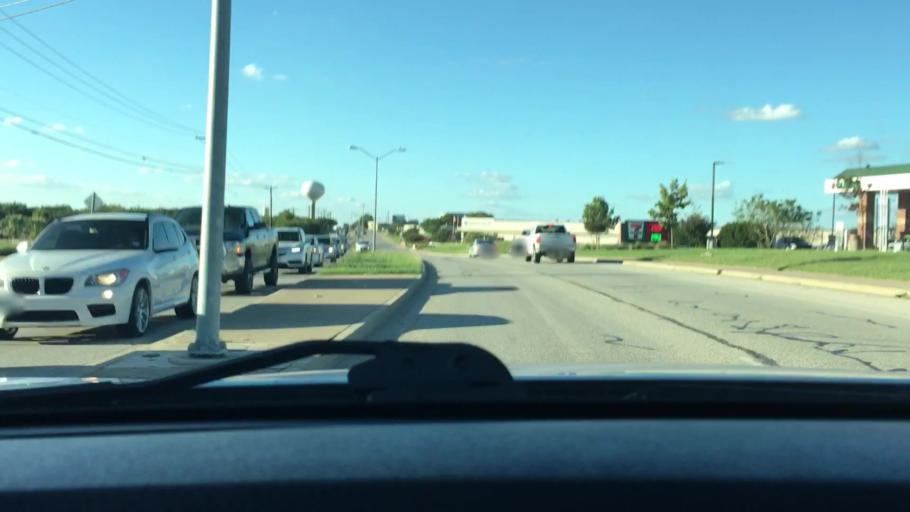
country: US
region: Texas
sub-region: Travis County
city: Windemere
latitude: 30.4730
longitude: -97.6413
